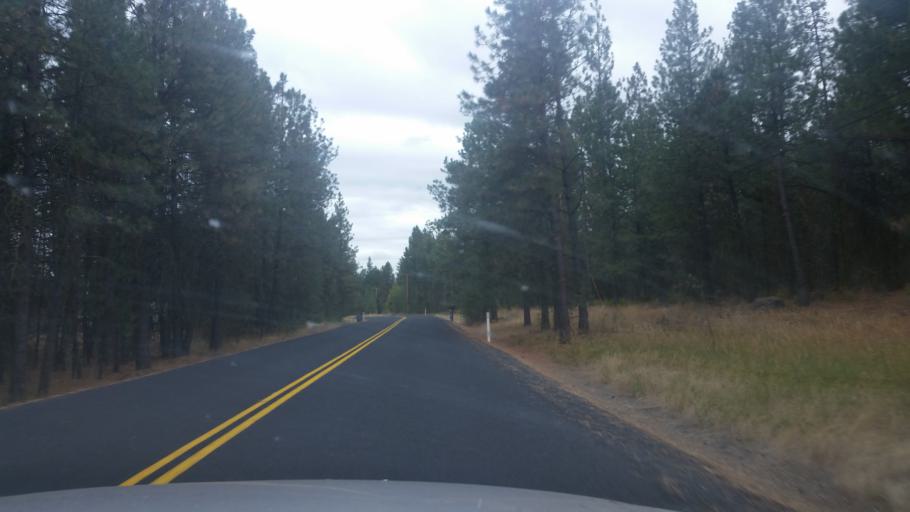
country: US
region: Washington
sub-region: Spokane County
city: Medical Lake
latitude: 47.5059
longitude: -117.7700
